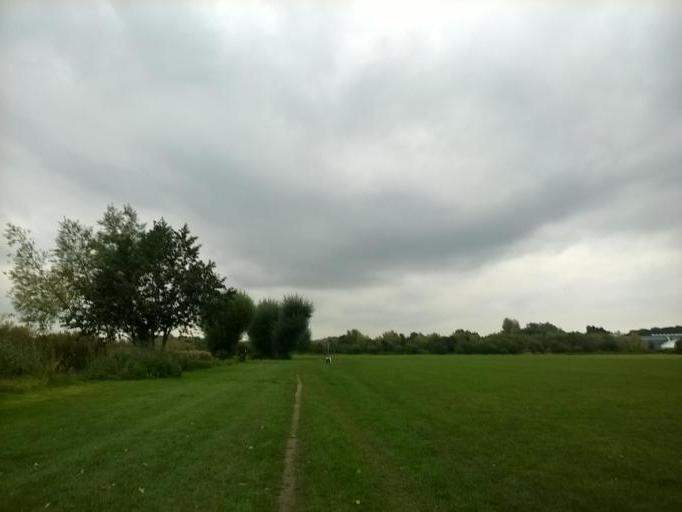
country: GB
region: England
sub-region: Wokingham
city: Earley
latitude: 51.4621
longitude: -0.9384
